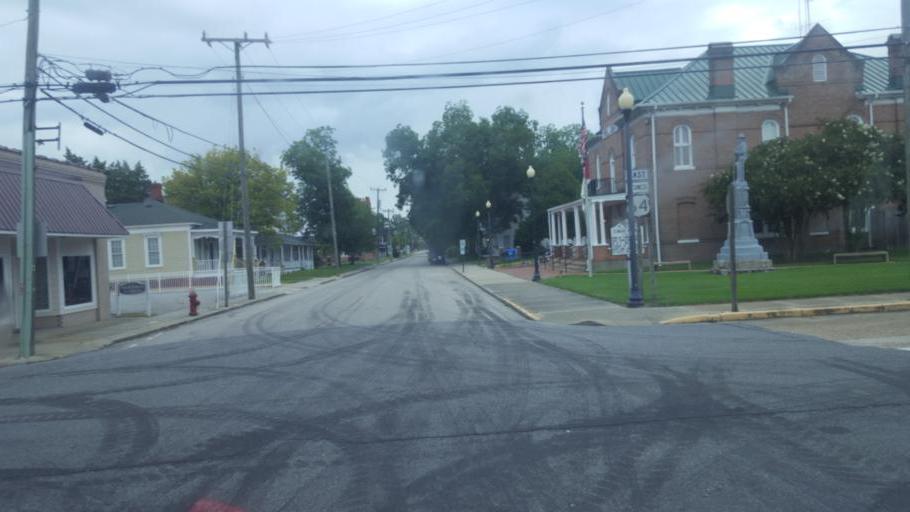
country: US
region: North Carolina
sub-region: Tyrrell County
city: Columbia
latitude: 35.9177
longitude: -76.2524
